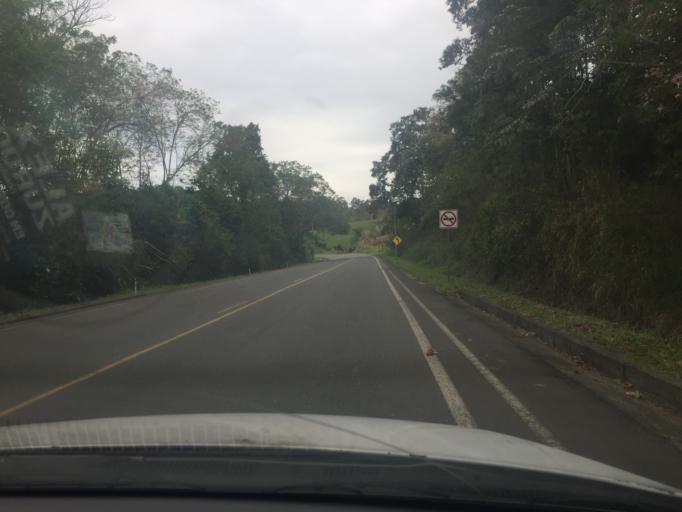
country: EC
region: Esmeraldas
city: Valdez
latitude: 1.0656
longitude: -79.1196
